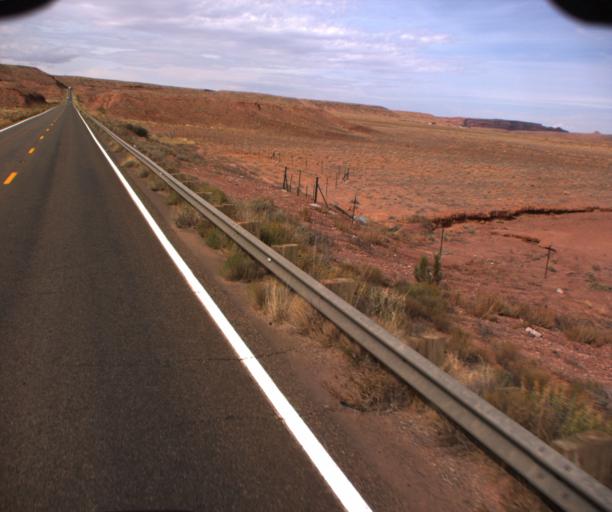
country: US
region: Arizona
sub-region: Apache County
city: Many Farms
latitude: 36.5379
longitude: -109.5185
